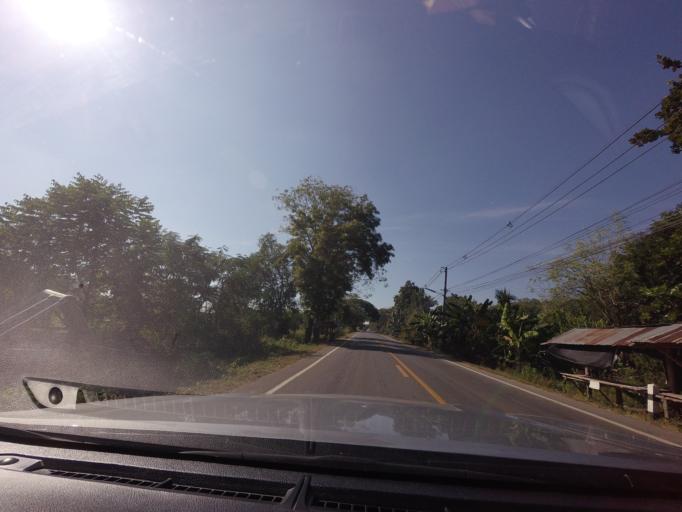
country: TH
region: Sukhothai
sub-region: Amphoe Si Satchanalai
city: Si Satchanalai
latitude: 17.6310
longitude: 99.6968
